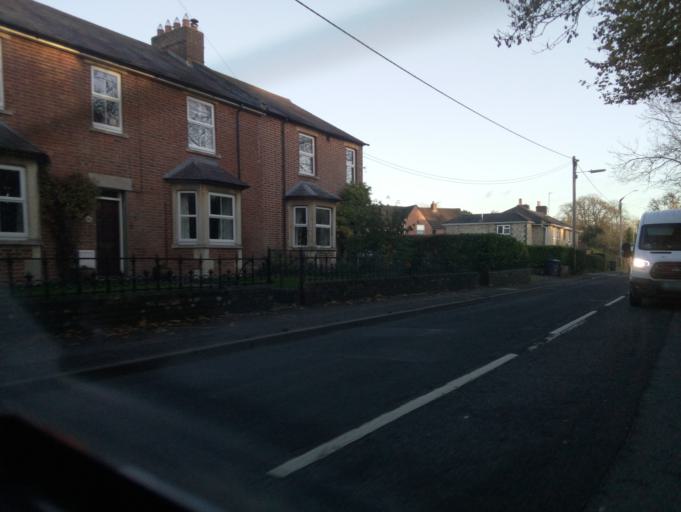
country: GB
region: England
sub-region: Wiltshire
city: Warminster
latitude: 51.2105
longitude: -2.1921
